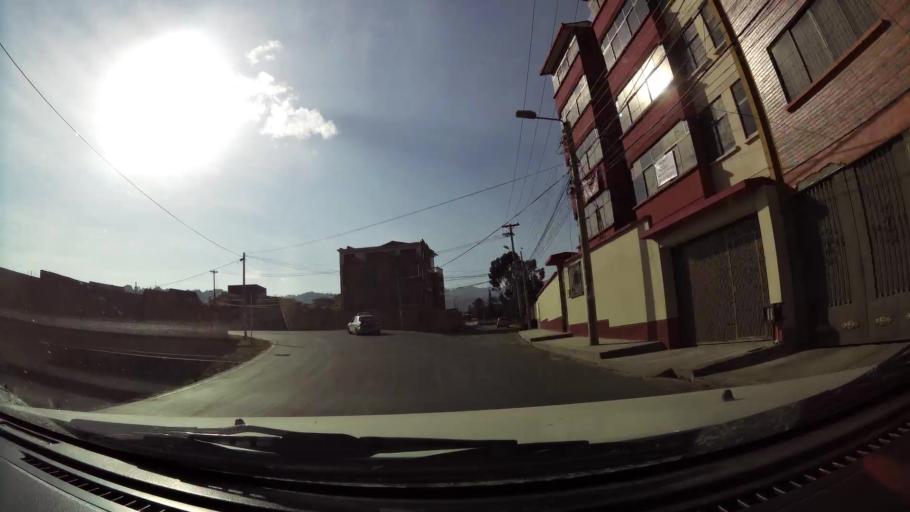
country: BO
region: La Paz
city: La Paz
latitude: -16.5221
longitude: -68.0803
